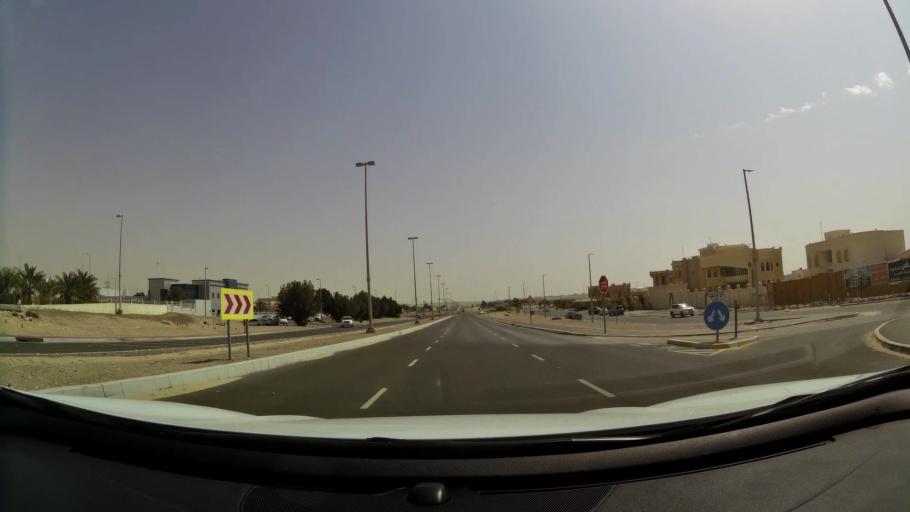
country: AE
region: Abu Dhabi
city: Abu Dhabi
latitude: 24.2932
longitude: 54.6568
